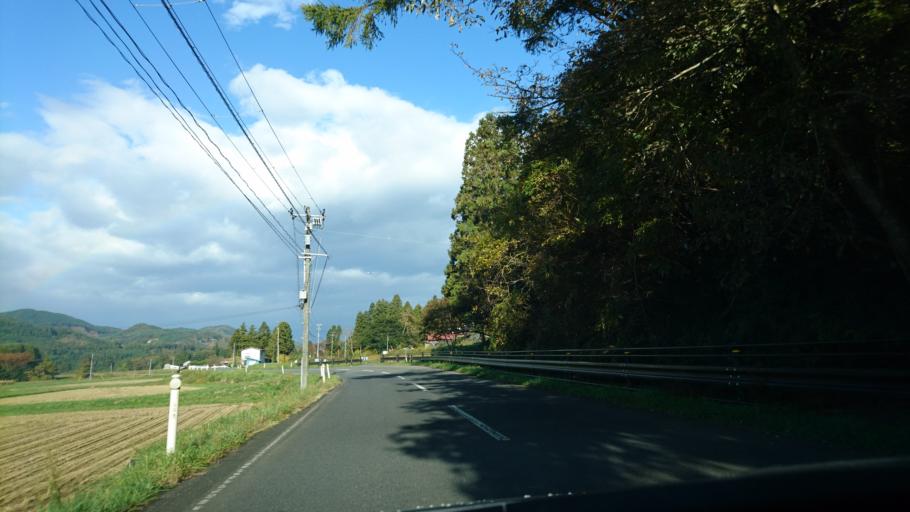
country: JP
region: Iwate
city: Mizusawa
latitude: 39.0474
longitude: 141.0523
